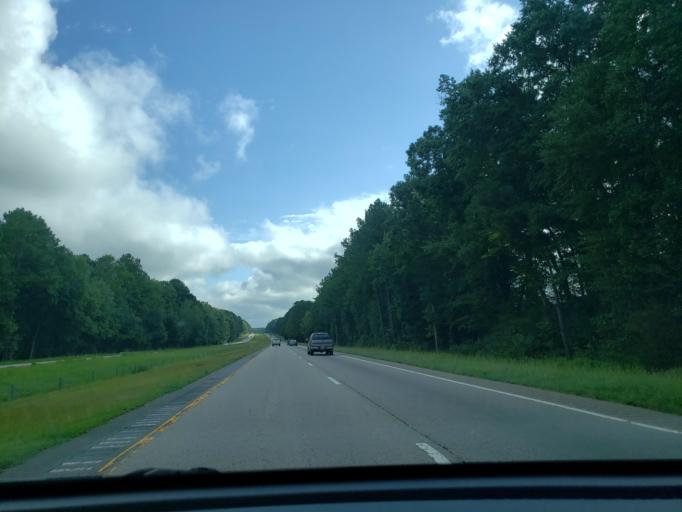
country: US
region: North Carolina
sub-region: Wake County
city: Zebulon
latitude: 35.8421
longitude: -78.2954
